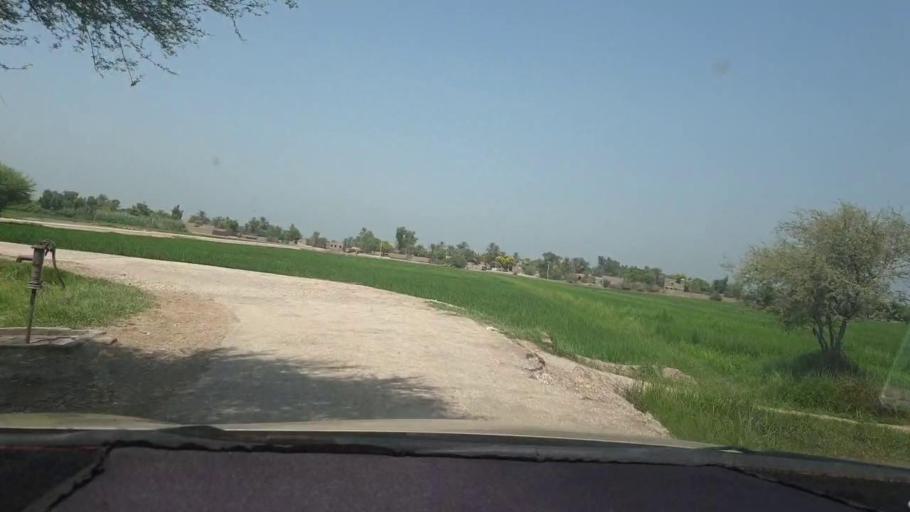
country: PK
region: Sindh
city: Kambar
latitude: 27.6219
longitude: 68.0533
